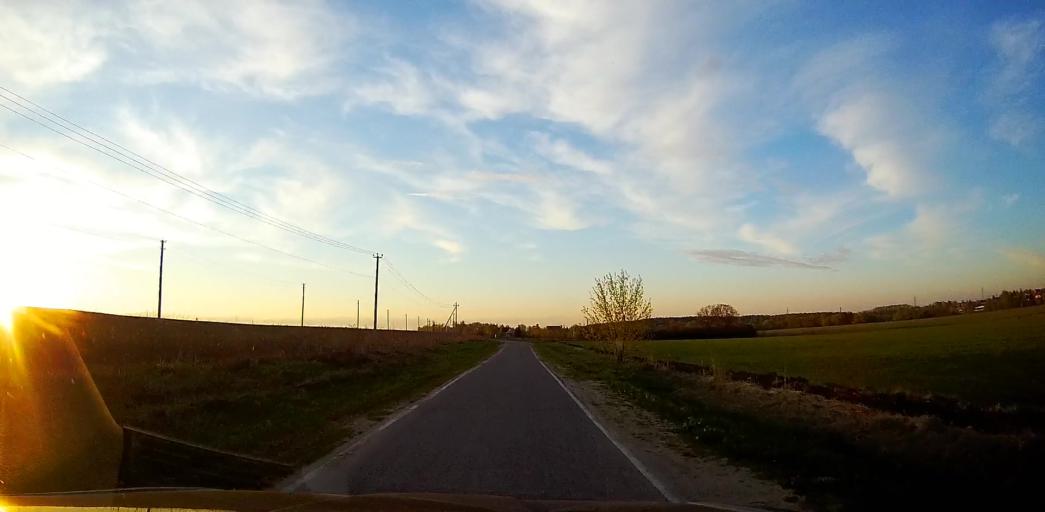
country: RU
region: Moskovskaya
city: Peski
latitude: 55.2235
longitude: 38.7361
